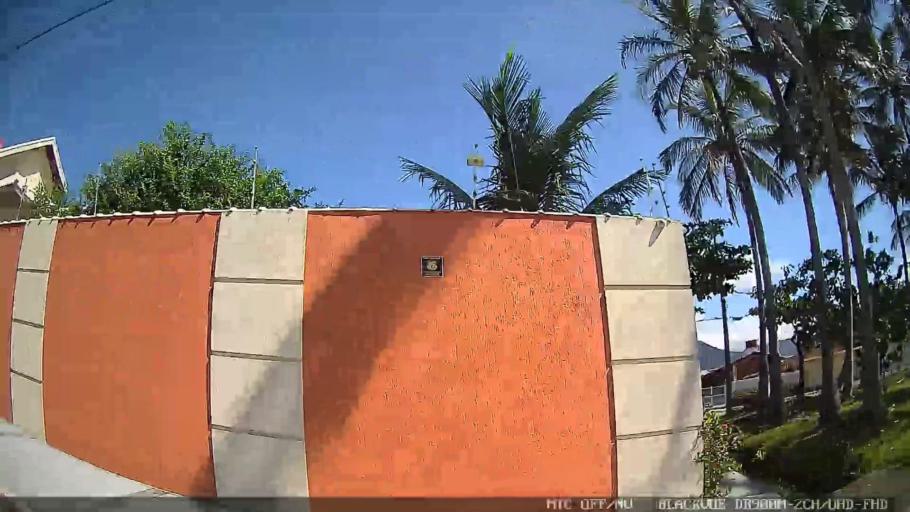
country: BR
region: Sao Paulo
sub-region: Peruibe
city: Peruibe
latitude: -24.3161
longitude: -46.9884
